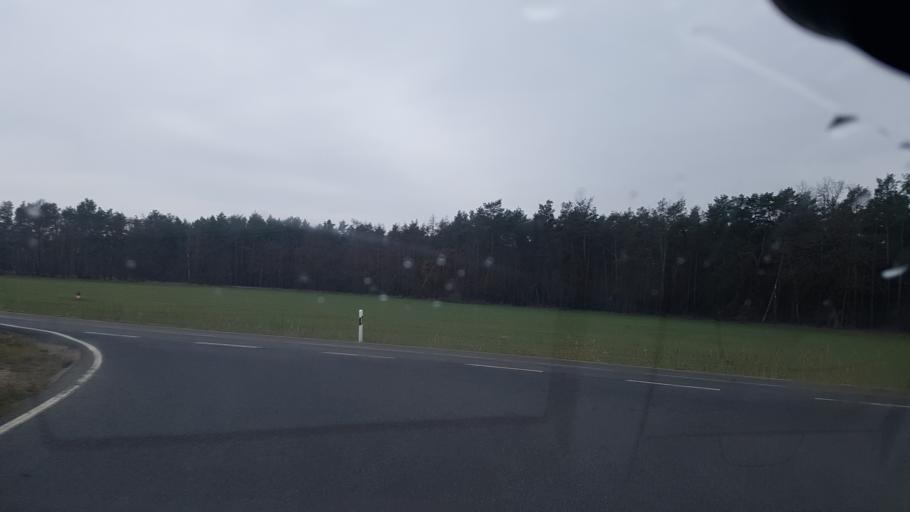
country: DE
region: Brandenburg
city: Cottbus
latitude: 51.7515
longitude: 14.4116
